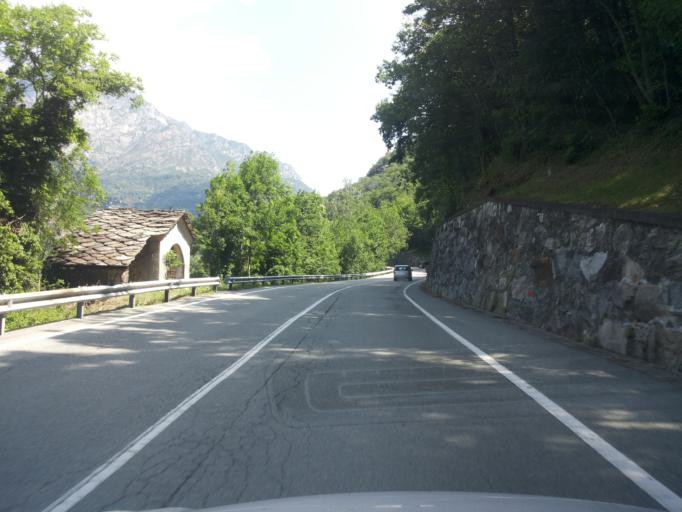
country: IT
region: Aosta Valley
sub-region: Valle d'Aosta
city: Pont-Saint-Martin
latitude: 45.6012
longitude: 7.8050
